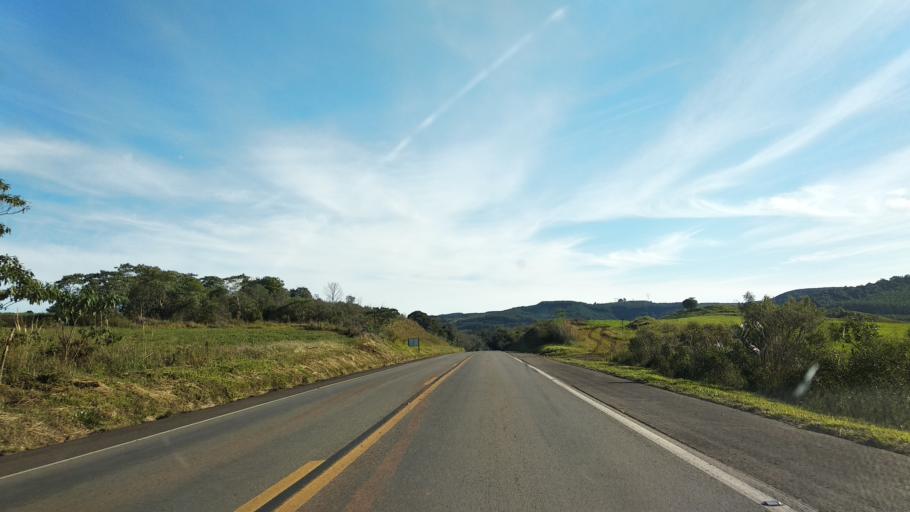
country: BR
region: Santa Catarina
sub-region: Celso Ramos
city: Celso Ramos
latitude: -27.5465
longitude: -51.4304
